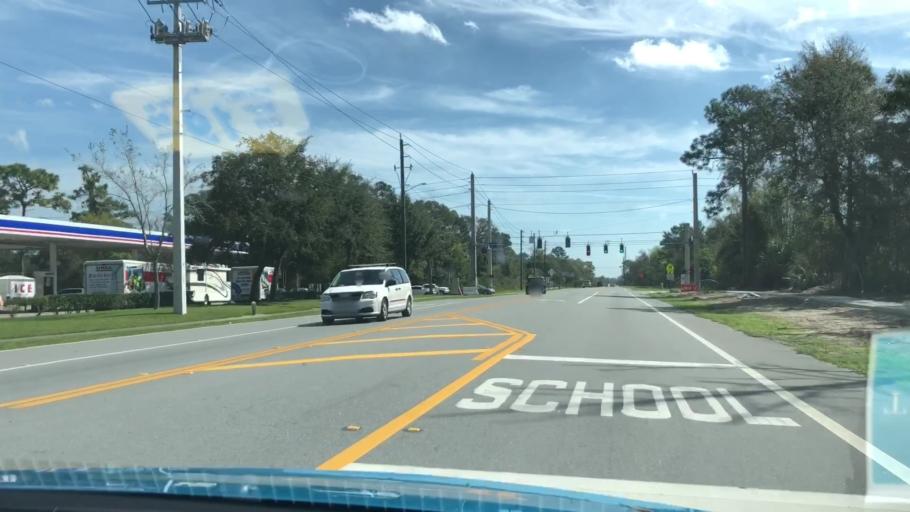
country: US
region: Florida
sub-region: Seminole County
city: Midway
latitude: 28.8567
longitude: -81.1872
